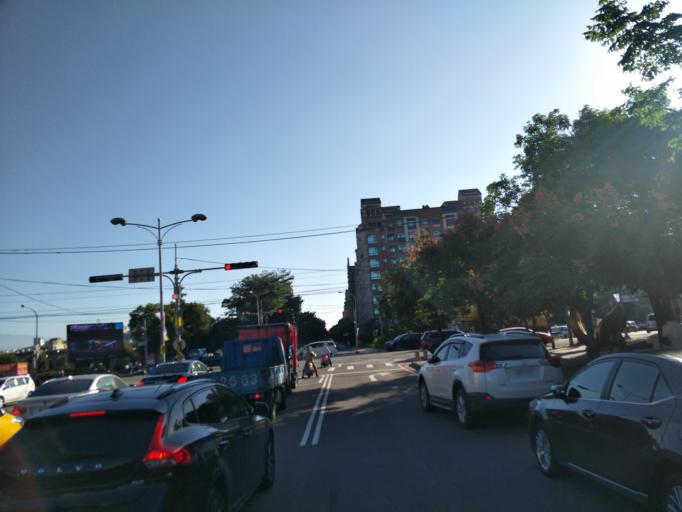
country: TW
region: Taiwan
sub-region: Hsinchu
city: Zhubei
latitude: 24.8361
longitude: 121.0204
